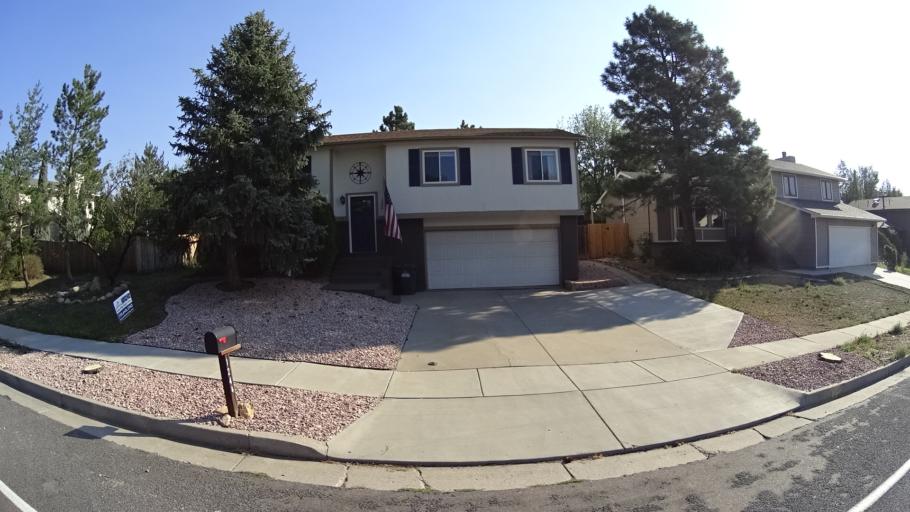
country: US
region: Colorado
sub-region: El Paso County
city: Stratmoor
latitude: 38.7786
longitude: -104.8048
